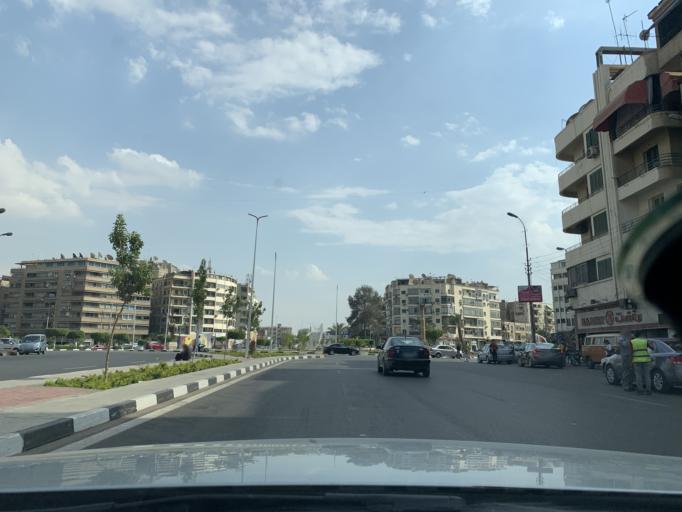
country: EG
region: Muhafazat al Qahirah
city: Cairo
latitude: 30.1015
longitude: 31.3432
